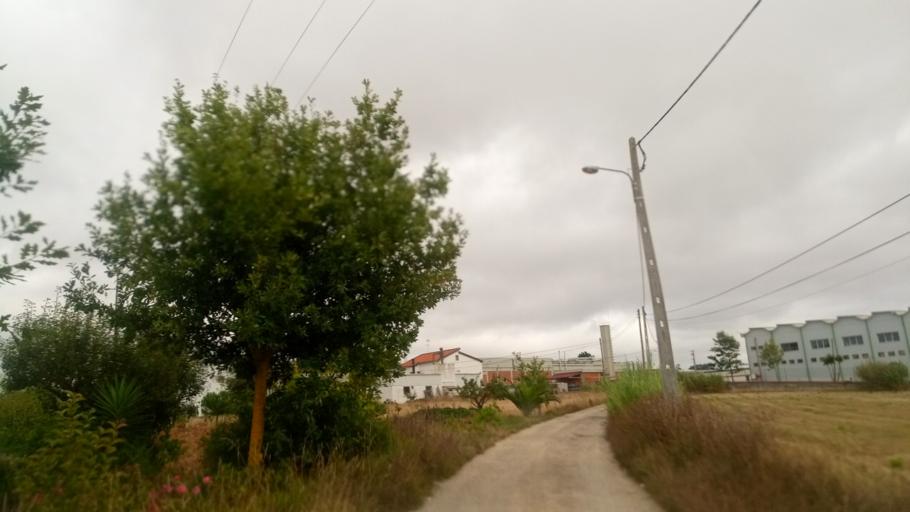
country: PT
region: Leiria
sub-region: Caldas da Rainha
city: Caldas da Rainha
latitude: 39.4283
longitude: -9.1345
